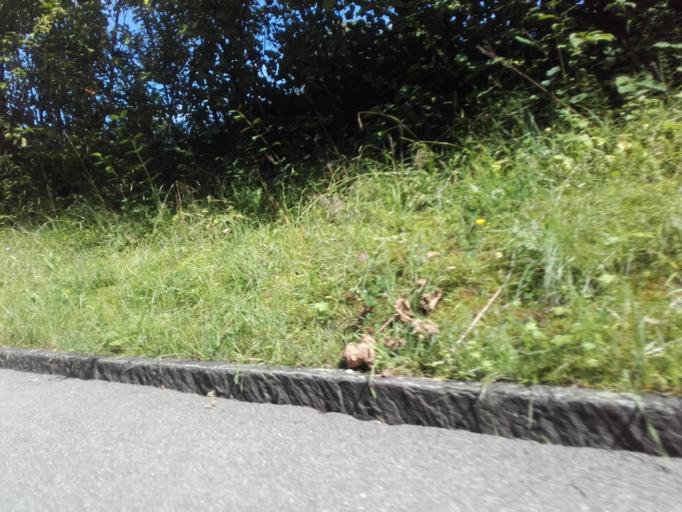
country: CH
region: Solothurn
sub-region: Bezirk Lebern
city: Riedholz
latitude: 47.2270
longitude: 7.5642
